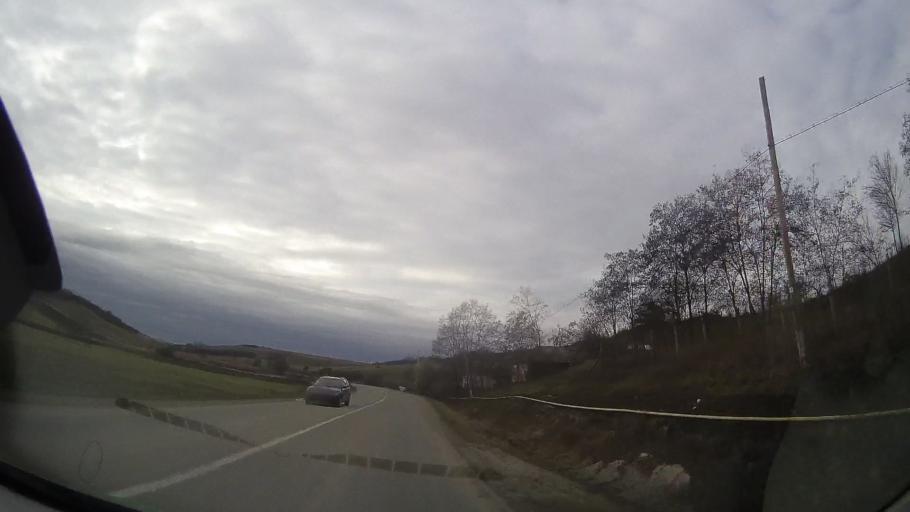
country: RO
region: Bistrita-Nasaud
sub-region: Comuna Budesti
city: Budesti
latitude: 46.8649
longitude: 24.2459
